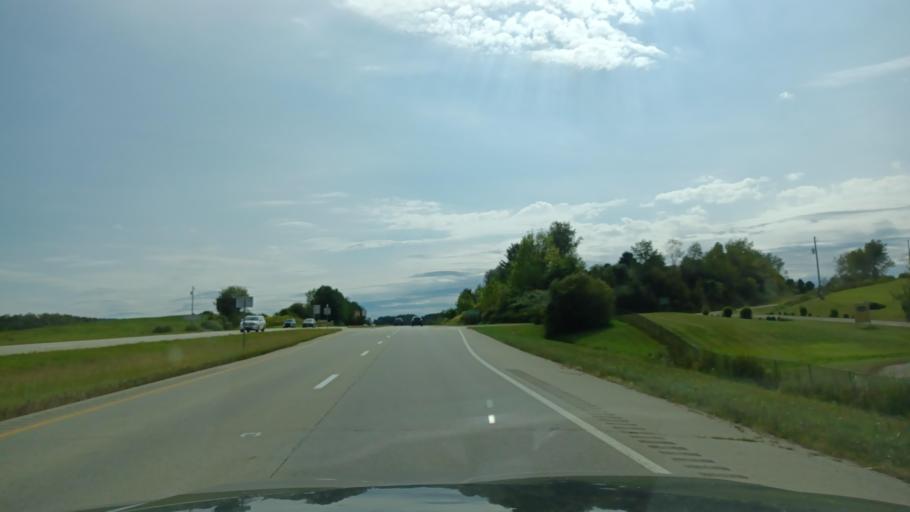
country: US
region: Ohio
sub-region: Athens County
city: Athens
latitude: 39.2757
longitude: -82.1578
